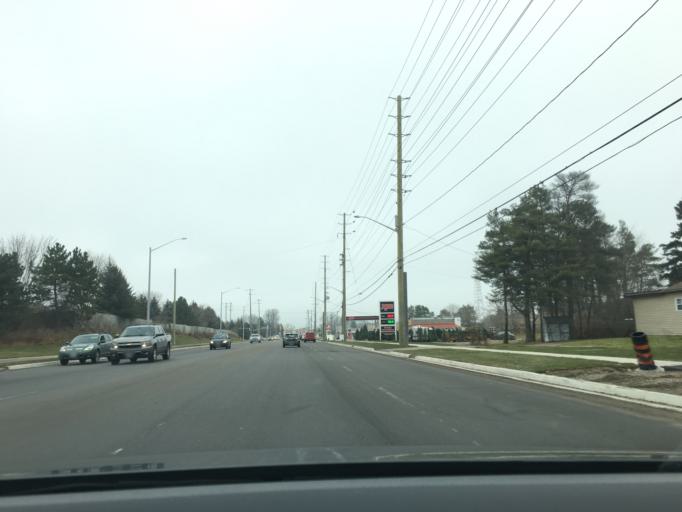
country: CA
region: Ontario
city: Barrie
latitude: 44.3444
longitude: -79.7058
